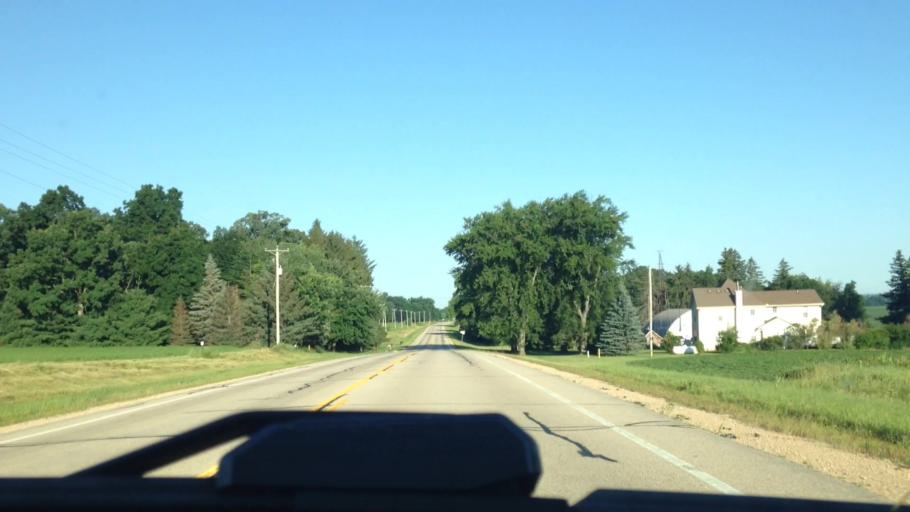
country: US
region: Wisconsin
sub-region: Dane County
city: De Forest
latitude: 43.3324
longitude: -89.2945
